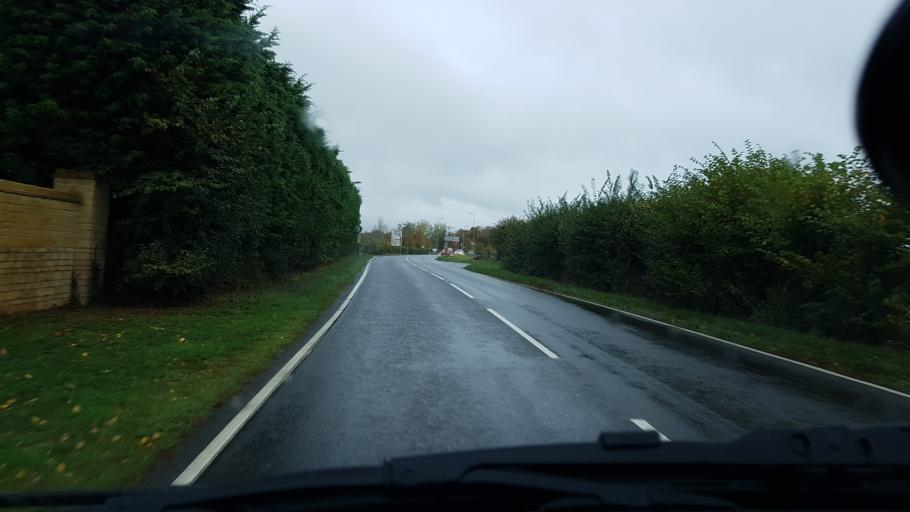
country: GB
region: England
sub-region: Oxfordshire
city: Frilford
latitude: 51.6765
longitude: -1.3982
